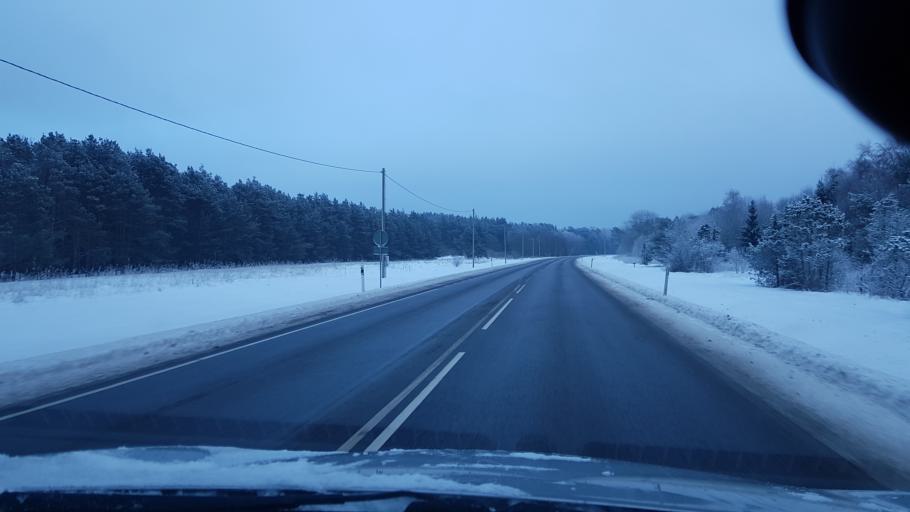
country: EE
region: Harju
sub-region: Paldiski linn
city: Paldiski
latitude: 59.3394
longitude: 24.2092
